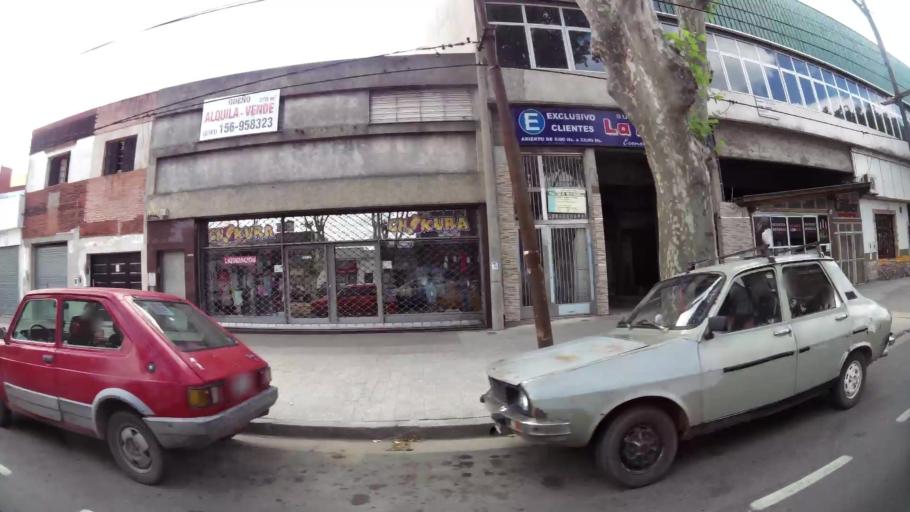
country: AR
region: Santa Fe
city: Gobernador Galvez
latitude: -32.9914
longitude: -60.6470
